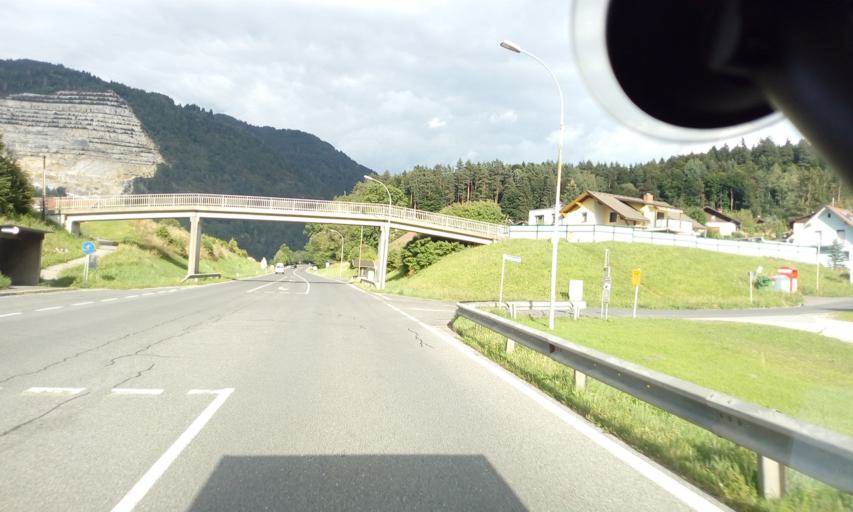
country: AT
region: Carinthia
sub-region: Villach Stadt
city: Villach
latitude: 46.6489
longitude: 13.7792
